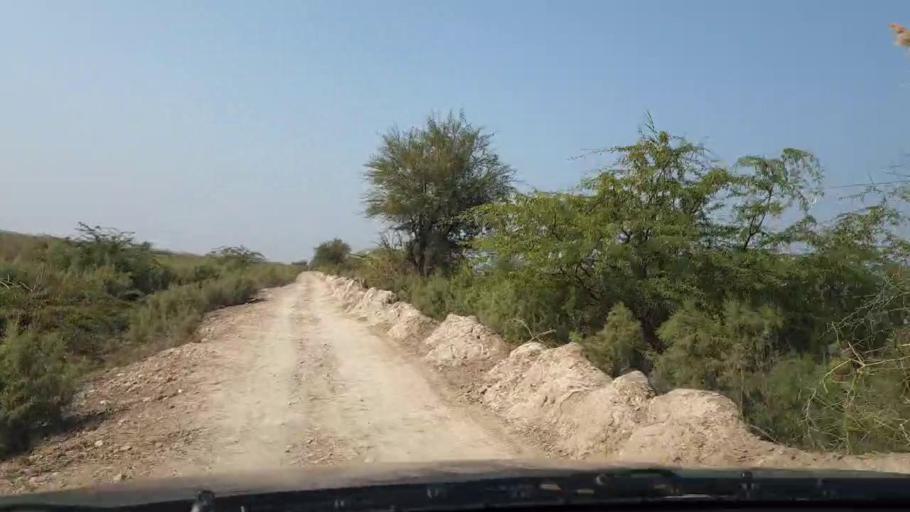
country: PK
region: Sindh
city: Jhol
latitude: 25.8873
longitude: 68.9826
